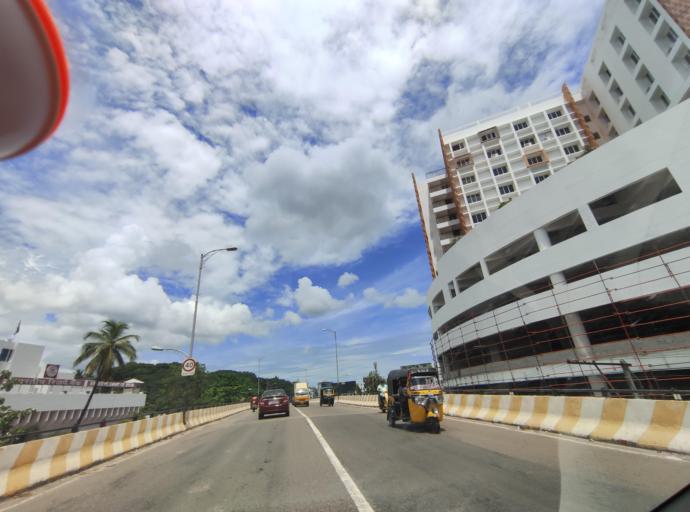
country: IN
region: Kerala
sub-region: Thiruvananthapuram
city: Thiruvananthapuram
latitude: 8.5019
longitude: 76.9534
